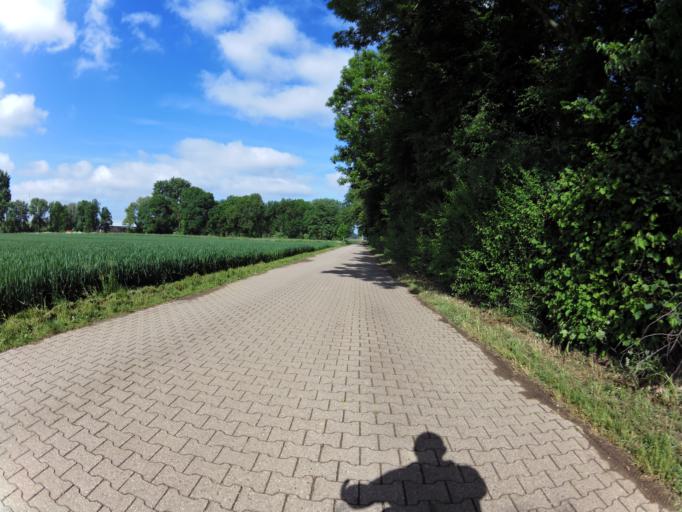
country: DE
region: North Rhine-Westphalia
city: Huckelhoven
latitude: 51.0160
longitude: 6.2262
